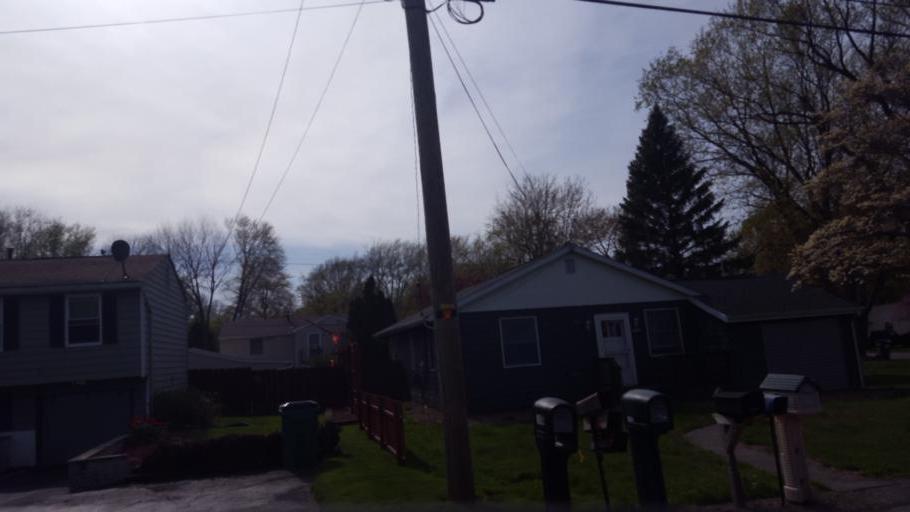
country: US
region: Ohio
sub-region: Lake County
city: North Madison
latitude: 41.8284
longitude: -81.0618
